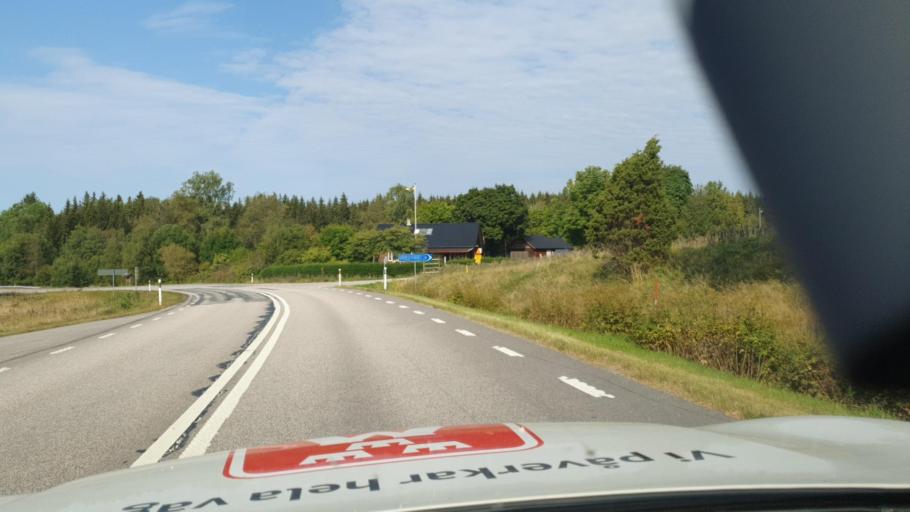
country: SE
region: Vaestra Goetaland
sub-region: Dals-Ed Kommun
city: Ed
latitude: 58.8510
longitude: 11.7150
